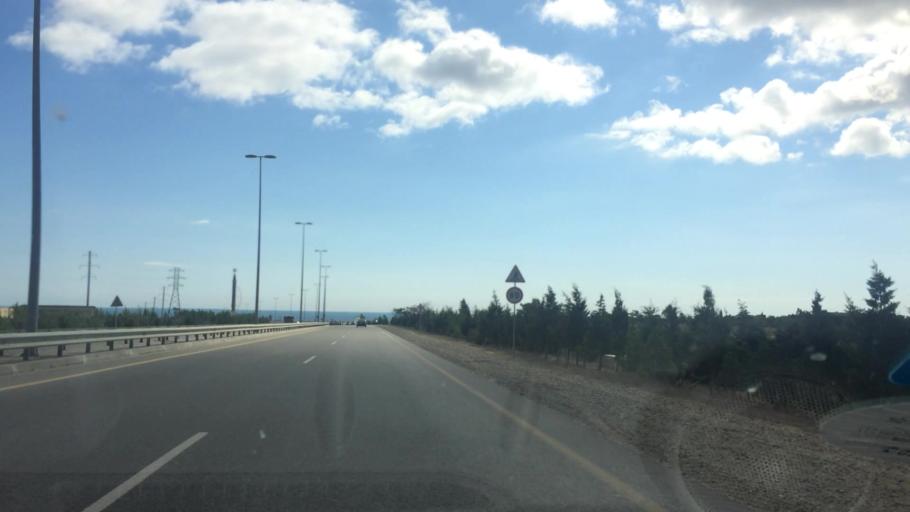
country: AZ
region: Baki
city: Zyrya
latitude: 40.4023
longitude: 50.3080
